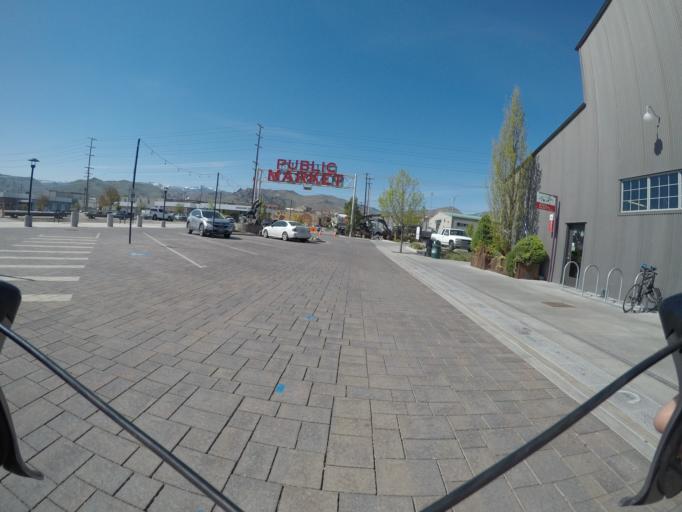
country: US
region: Washington
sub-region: Chelan County
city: Wenatchee
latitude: 47.4248
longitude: -120.3070
